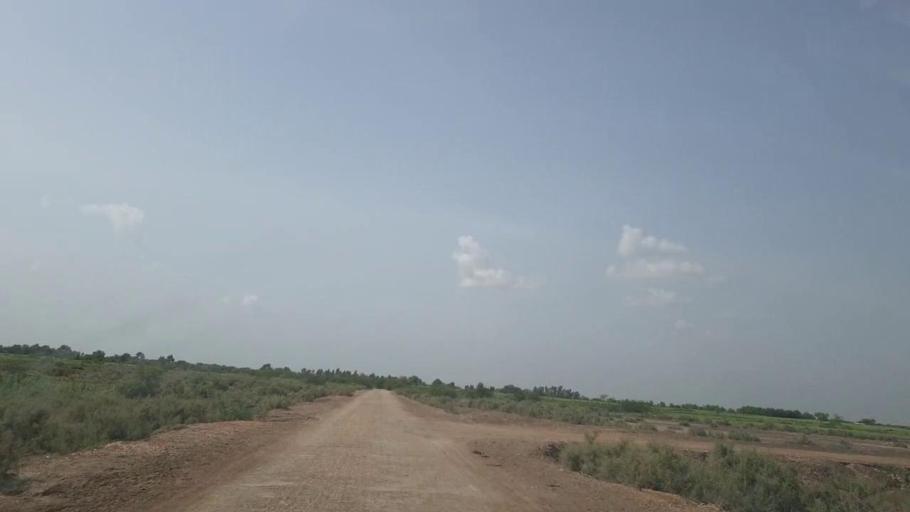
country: PK
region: Sindh
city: Tando Bago
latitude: 24.7759
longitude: 69.1306
